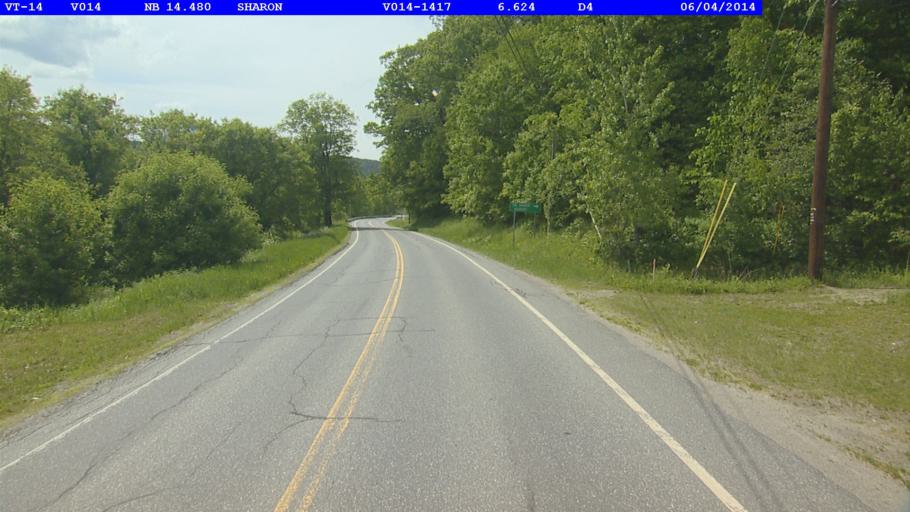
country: US
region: Vermont
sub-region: Windsor County
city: Woodstock
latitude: 43.7874
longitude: -72.4817
